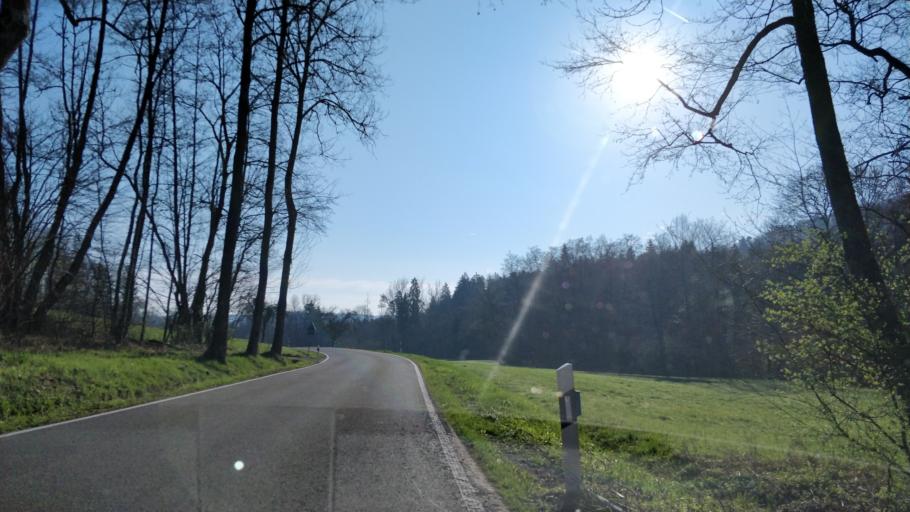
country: DE
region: Baden-Wuerttemberg
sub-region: Regierungsbezirk Stuttgart
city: Oberrot
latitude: 49.0482
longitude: 9.7085
